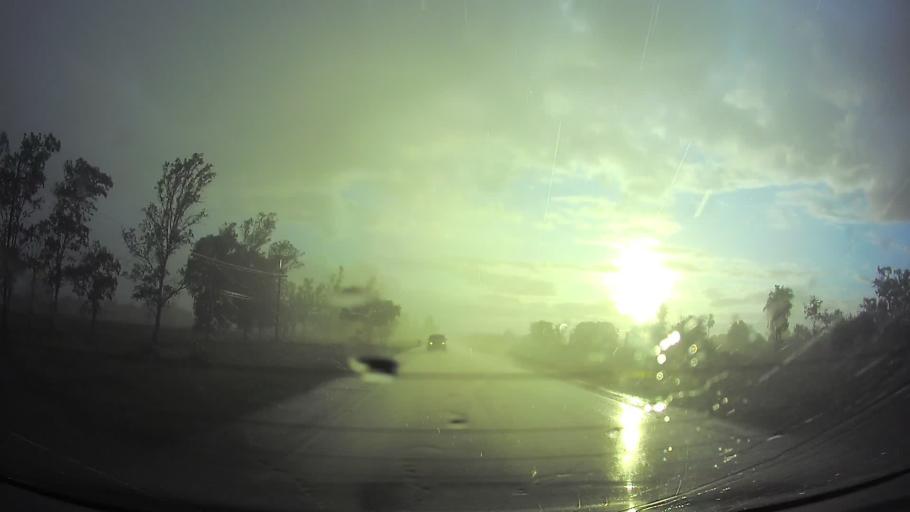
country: PY
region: Paraguari
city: Paraguari
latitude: -25.6998
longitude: -57.1773
